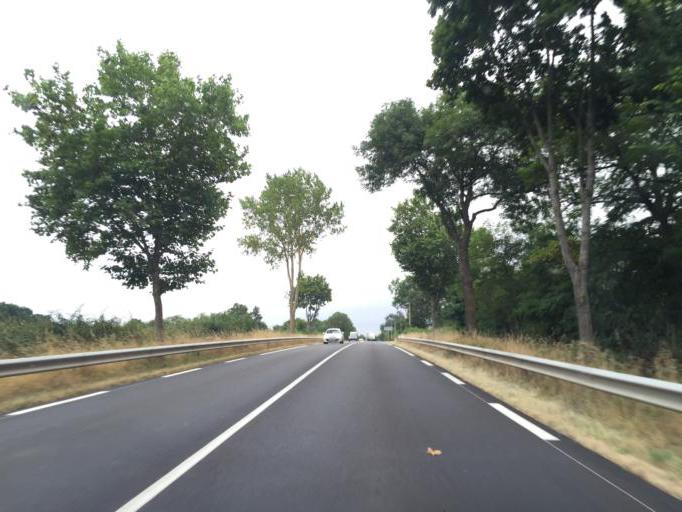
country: FR
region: Auvergne
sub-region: Departement de l'Allier
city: Brout-Vernet
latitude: 46.1990
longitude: 3.2718
